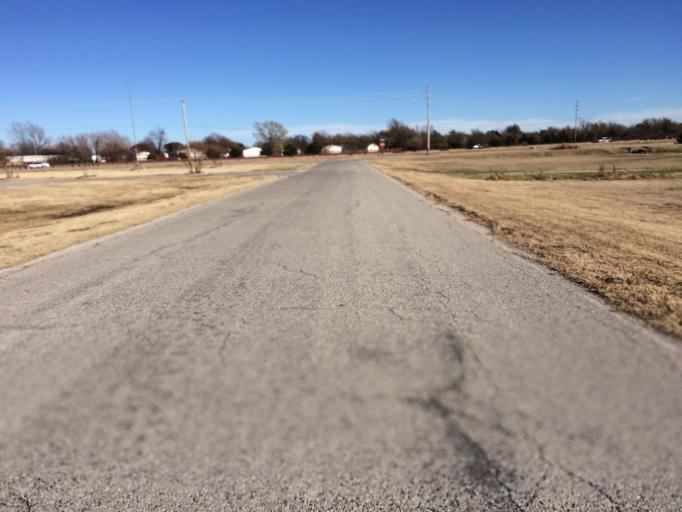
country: US
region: Oklahoma
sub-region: Cleveland County
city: Norman
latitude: 35.2379
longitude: -97.4566
